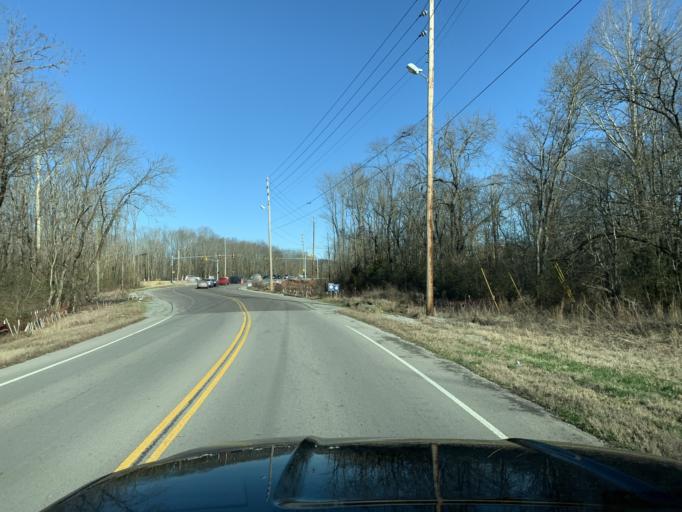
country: US
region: Tennessee
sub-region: Maury County
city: Spring Hill
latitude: 35.7512
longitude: -86.9215
